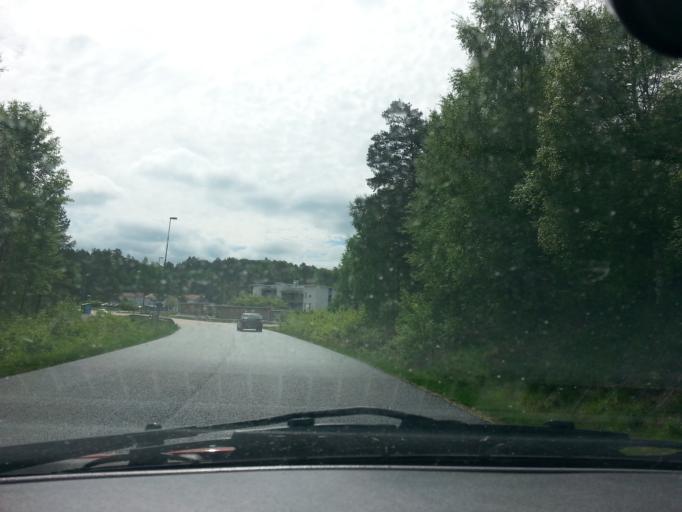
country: SE
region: Vaestra Goetaland
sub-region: Partille Kommun
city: Furulund
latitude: 57.7314
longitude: 12.1332
